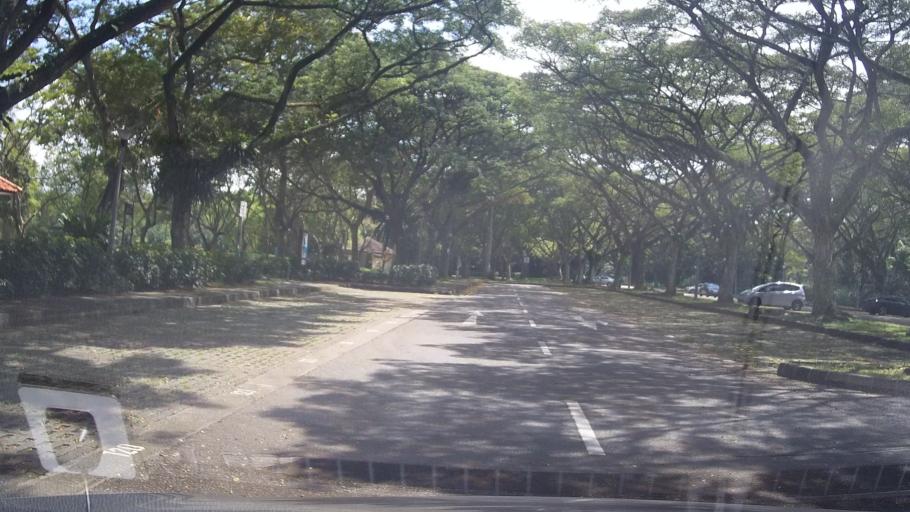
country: MY
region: Johor
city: Kampung Pasir Gudang Baru
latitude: 1.3786
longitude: 103.9483
